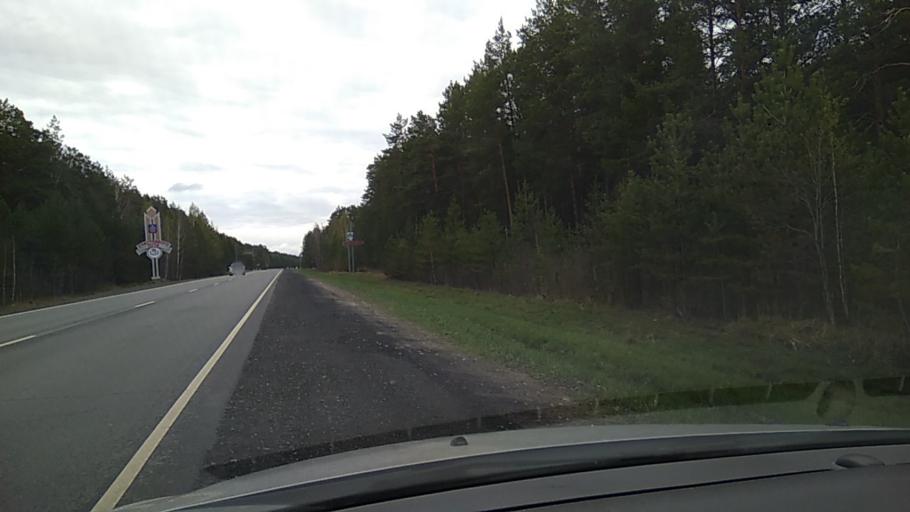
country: RU
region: Tjumen
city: Chervishevo
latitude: 56.8189
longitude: 65.3800
